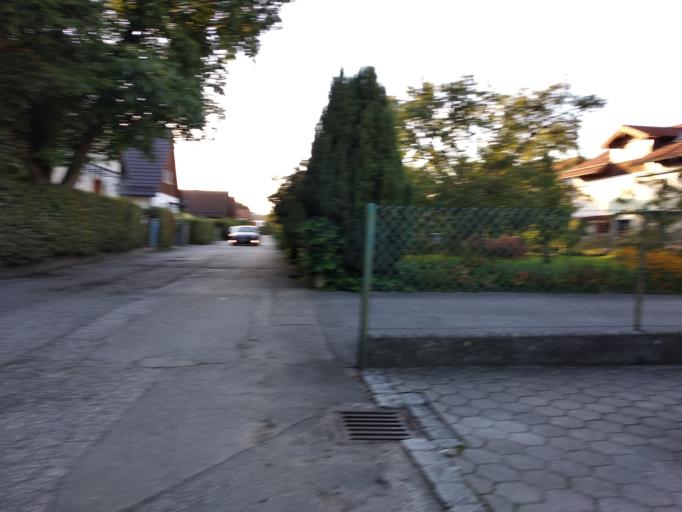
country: DE
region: Bavaria
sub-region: Upper Bavaria
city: Steinhoring
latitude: 48.0885
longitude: 12.0323
